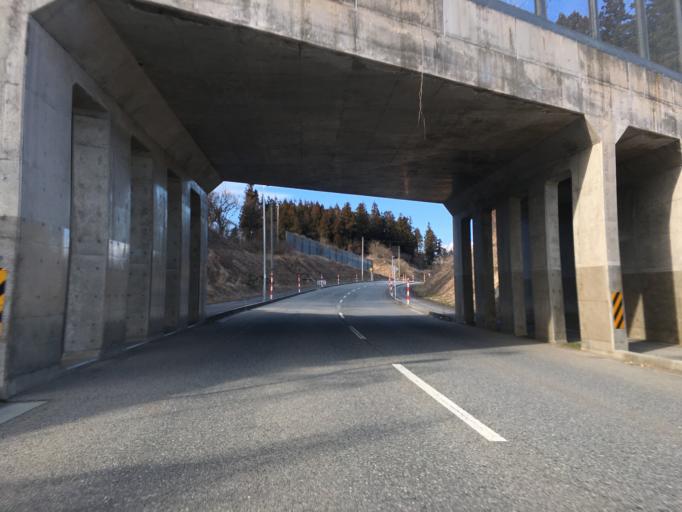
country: JP
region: Yamagata
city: Nagai
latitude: 38.0200
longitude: 139.9721
